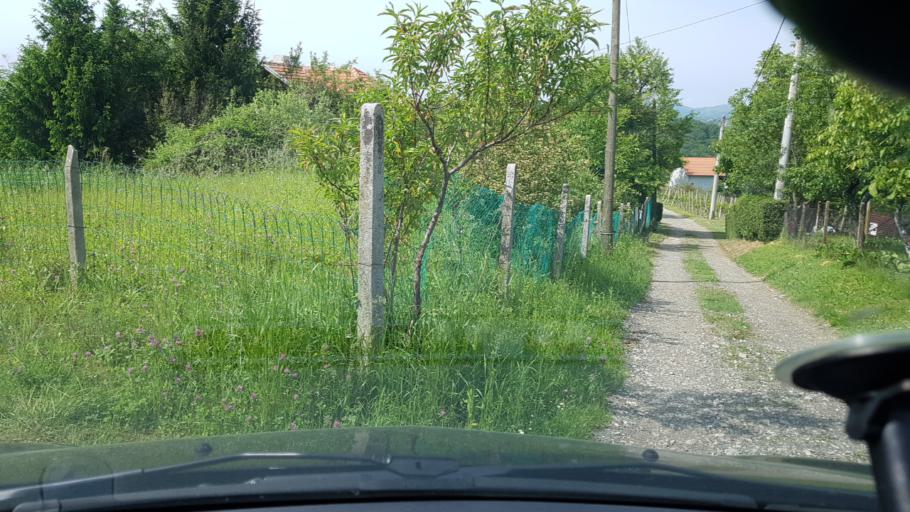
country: HR
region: Krapinsko-Zagorska
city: Marija Bistrica
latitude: 45.9386
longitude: 16.2120
